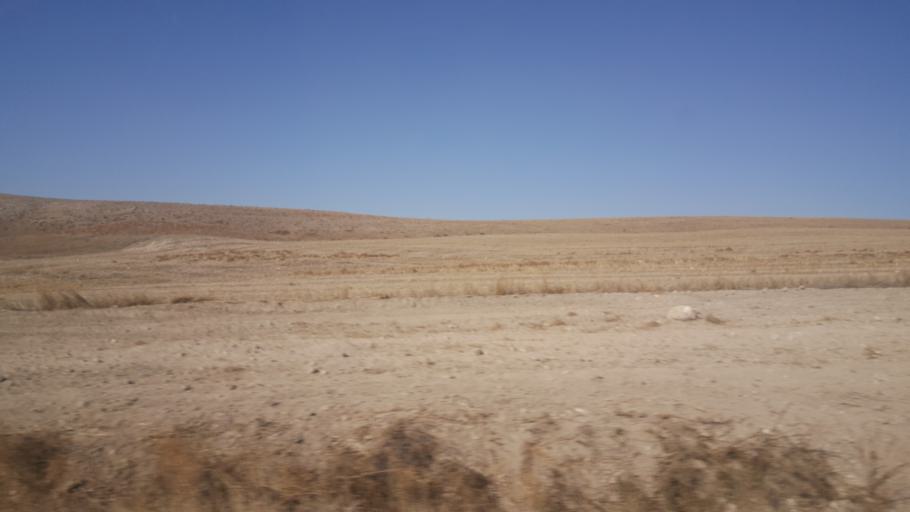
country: TR
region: Konya
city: Celtik
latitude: 39.0911
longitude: 32.0586
